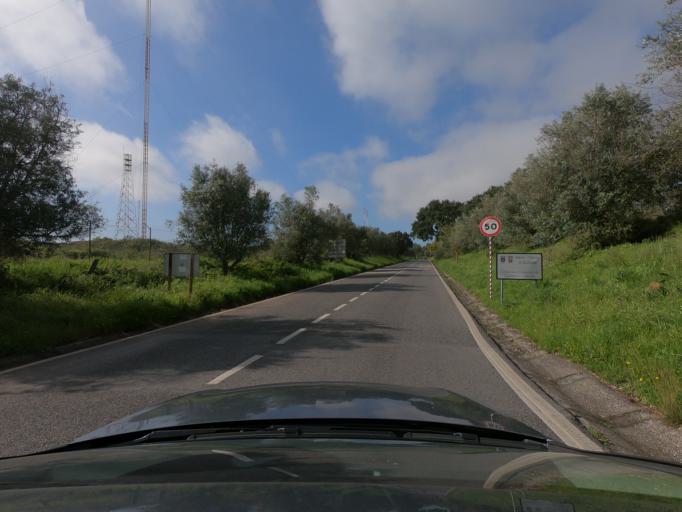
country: PT
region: Lisbon
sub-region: Oeiras
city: Quejas
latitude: 38.7269
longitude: -9.2702
